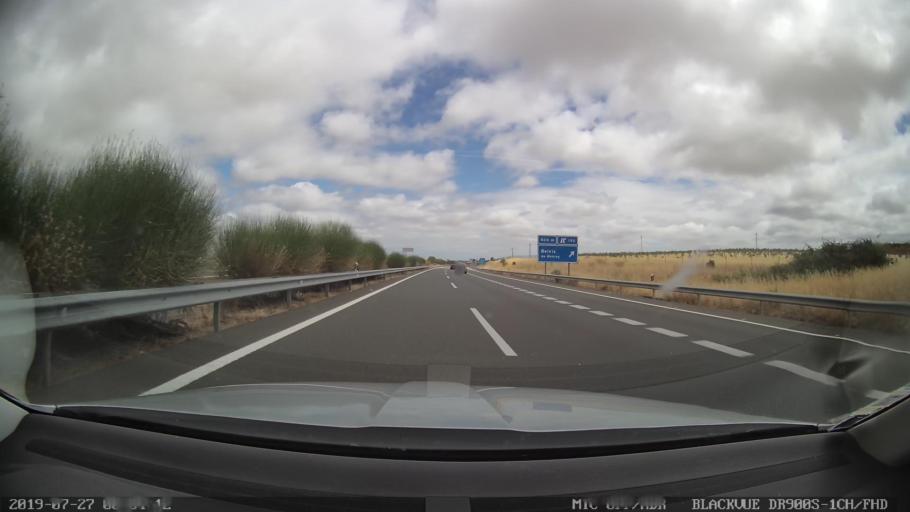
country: ES
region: Extremadura
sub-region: Provincia de Caceres
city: Almaraz
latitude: 39.8314
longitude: -5.6544
